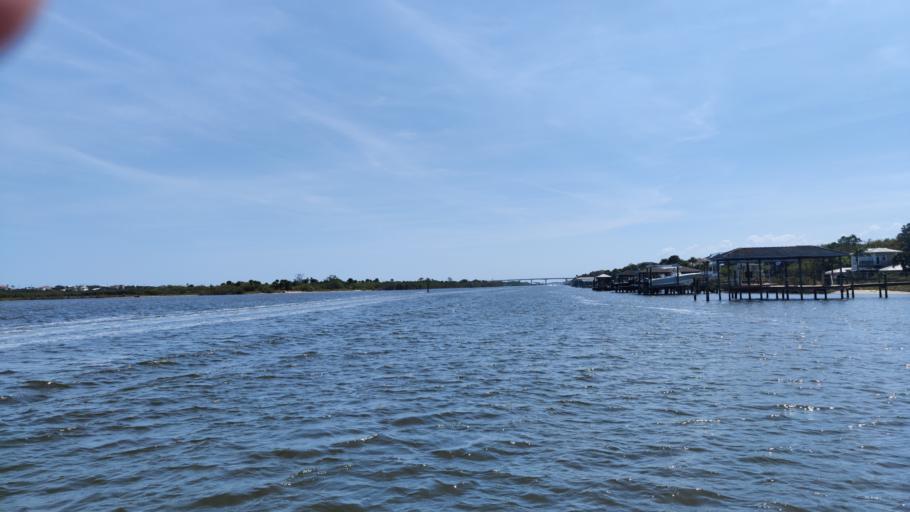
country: US
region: Florida
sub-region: Flagler County
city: Flagler Beach
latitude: 29.4973
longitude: -81.1435
